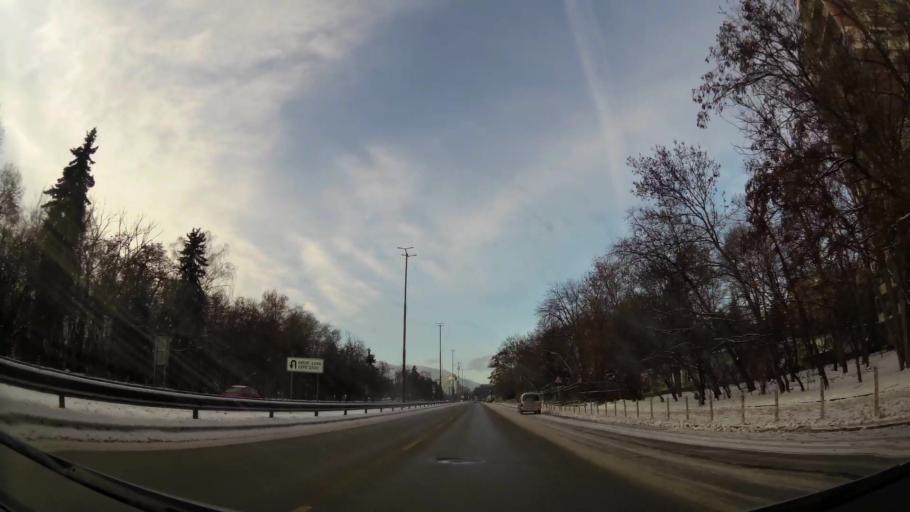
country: BG
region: Sofia-Capital
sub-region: Stolichna Obshtina
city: Sofia
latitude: 42.6665
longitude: 23.3230
